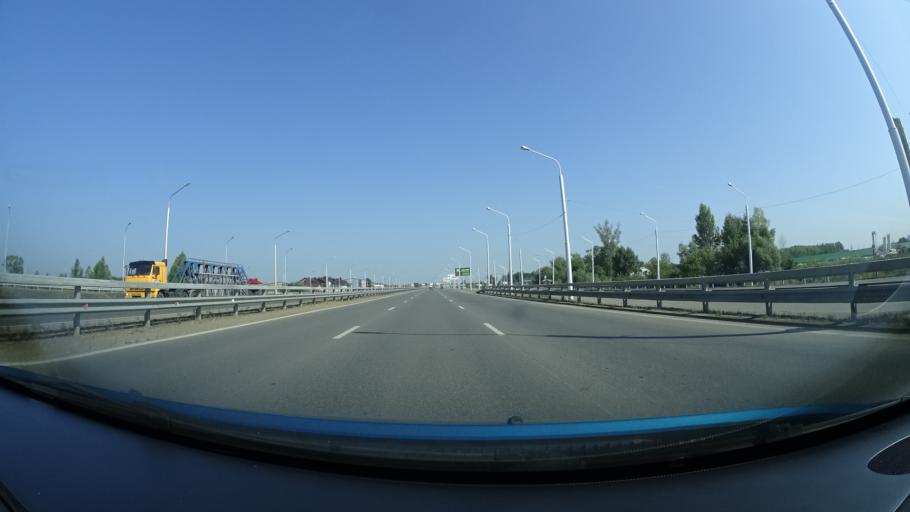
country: RU
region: Bashkortostan
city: Ufa
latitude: 54.7660
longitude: 55.9555
